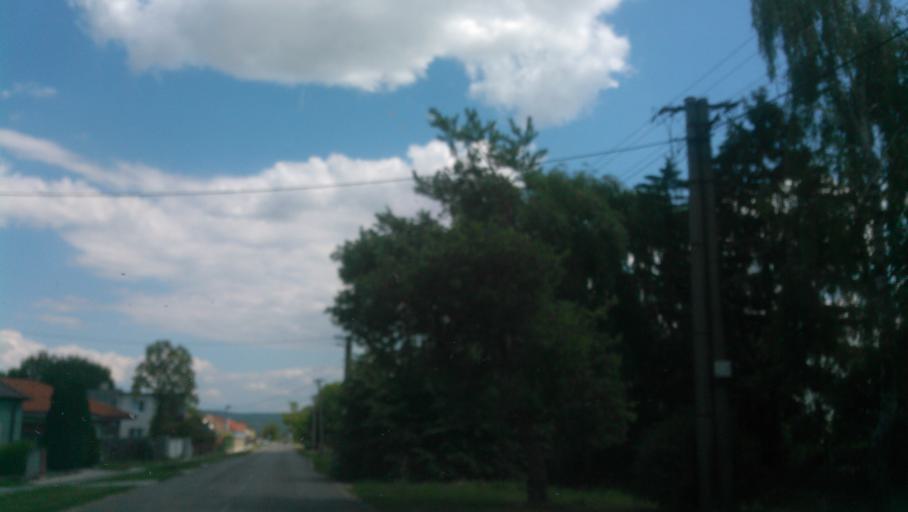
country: SK
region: Trnavsky
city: Leopoldov
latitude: 48.5073
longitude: 17.7267
